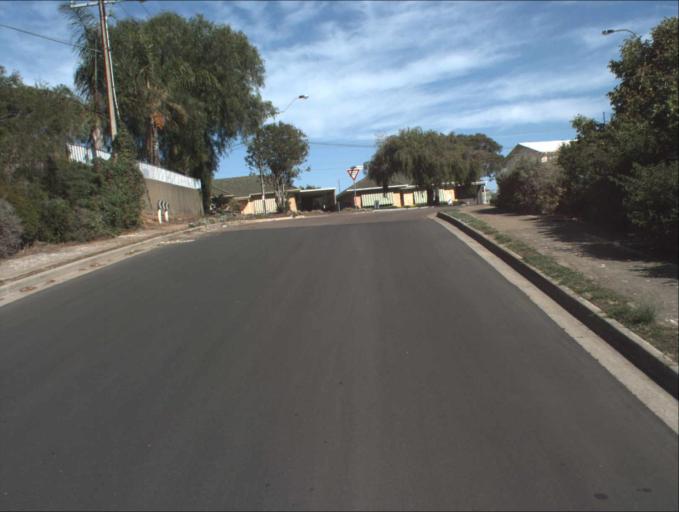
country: AU
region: South Australia
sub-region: Campbelltown
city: Paradise
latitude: -34.8670
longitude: 138.6549
